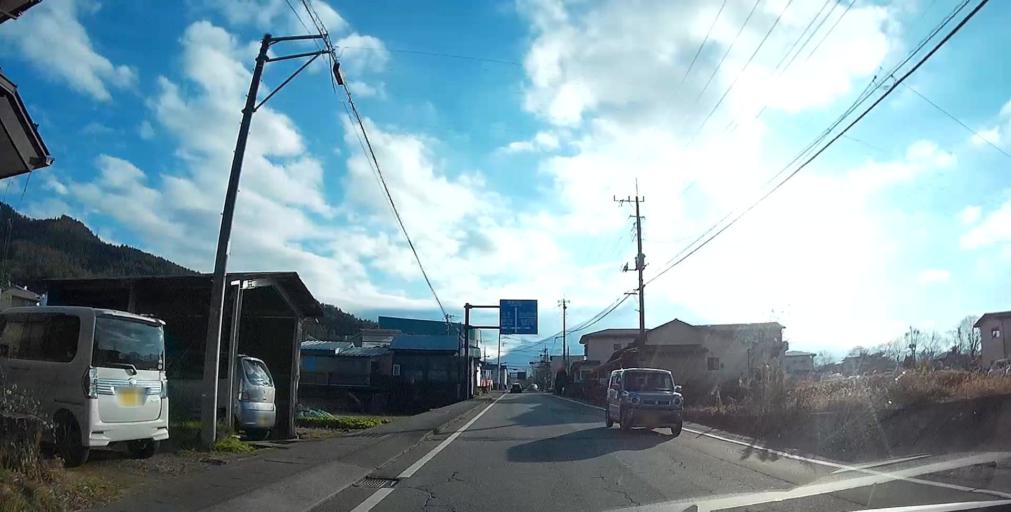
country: JP
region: Yamanashi
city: Fujikawaguchiko
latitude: 35.4788
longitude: 138.8165
